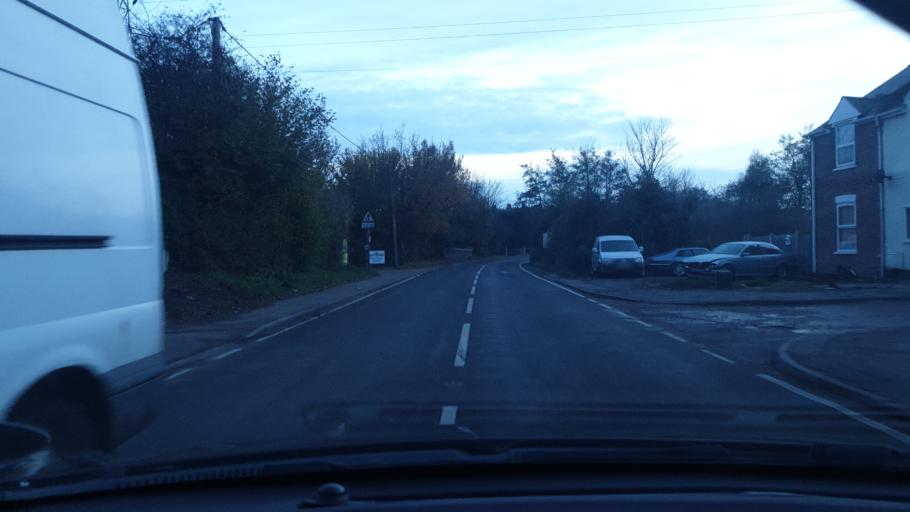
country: GB
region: England
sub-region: Essex
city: Little Clacton
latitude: 51.8471
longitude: 1.1631
